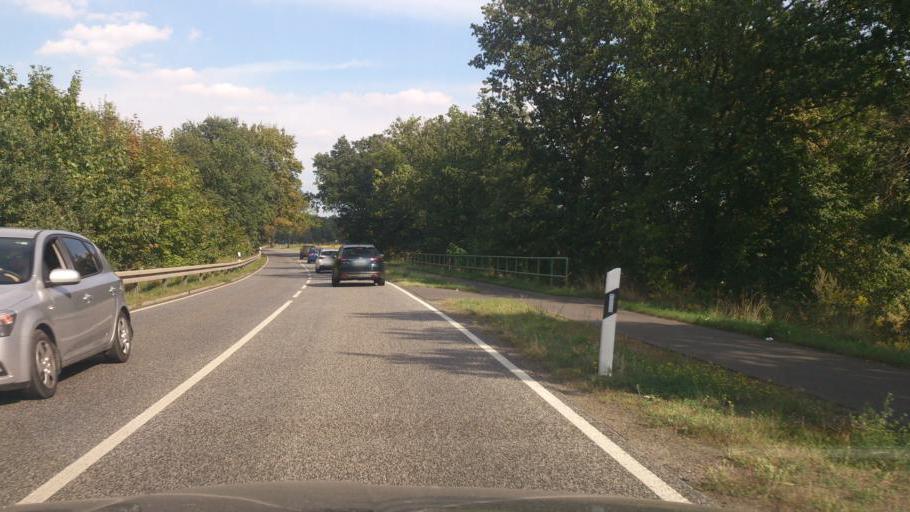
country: DE
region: Brandenburg
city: Ludwigsfelde
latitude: 52.3176
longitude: 13.2223
